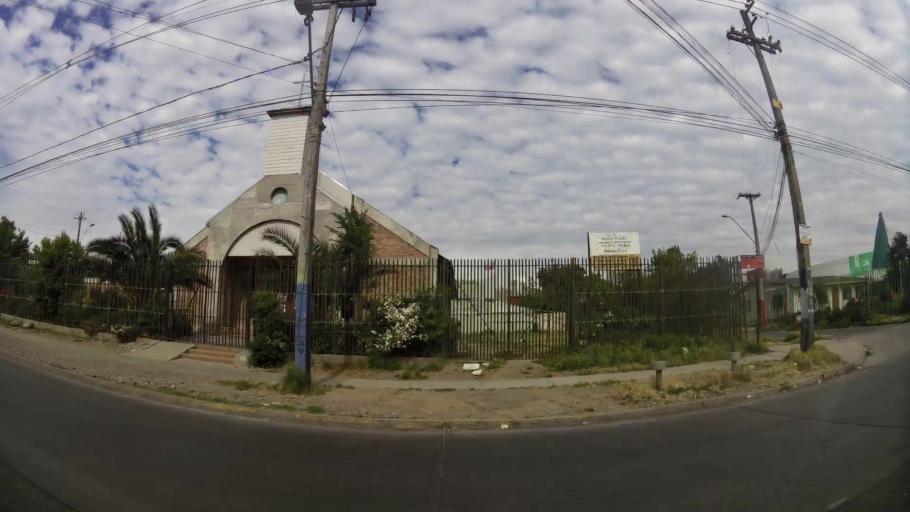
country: CL
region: Santiago Metropolitan
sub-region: Provincia de Santiago
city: La Pintana
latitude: -33.5856
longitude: -70.6393
